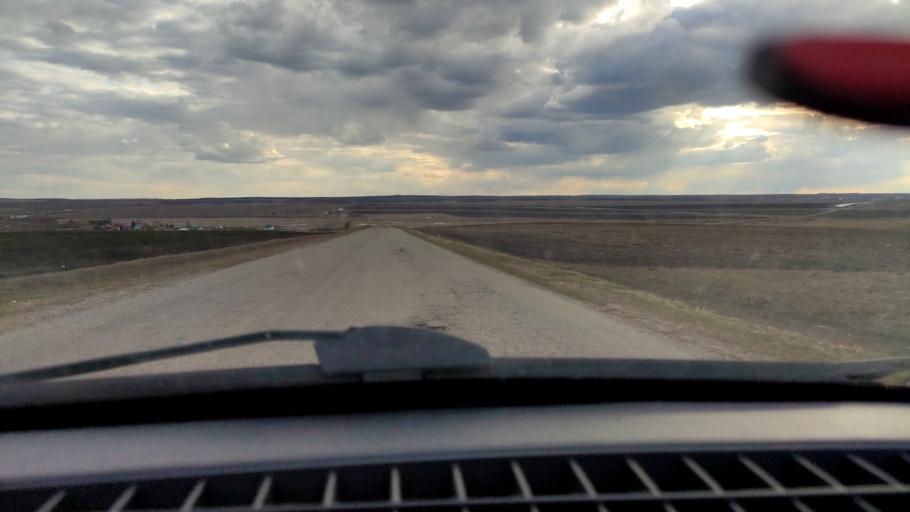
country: RU
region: Bashkortostan
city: Tolbazy
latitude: 54.2949
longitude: 55.9145
